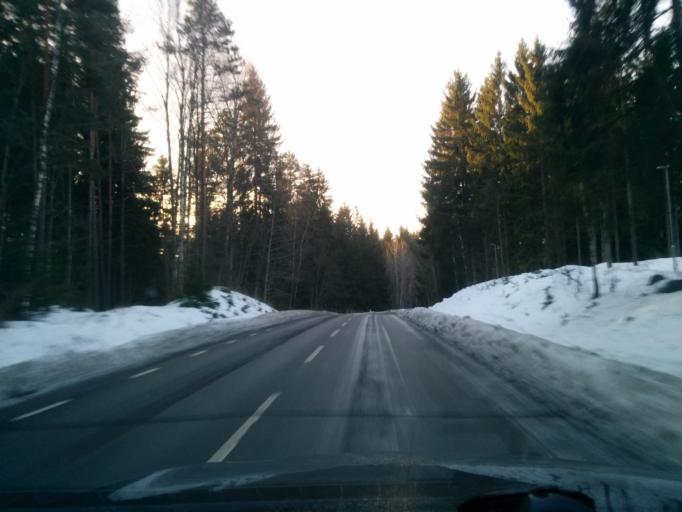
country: SE
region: Uppsala
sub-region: Tierps Kommun
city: Orbyhus
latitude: 60.2198
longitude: 17.7030
